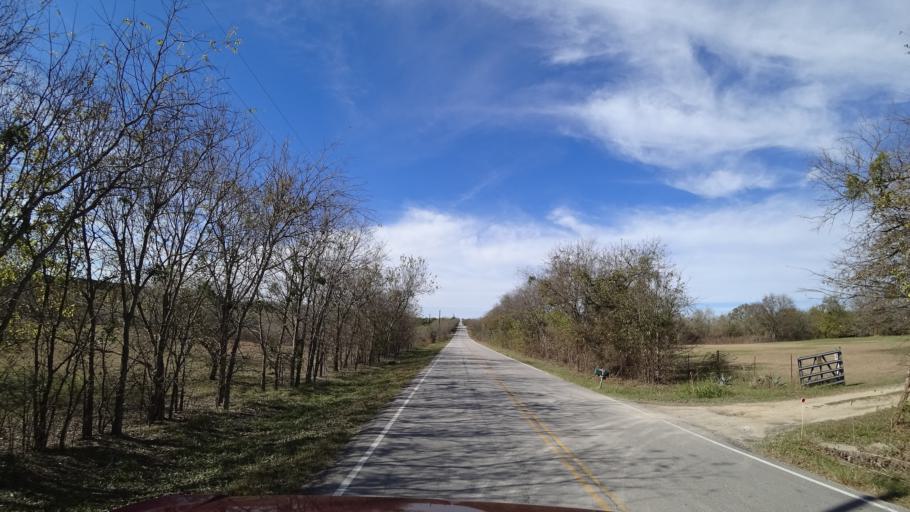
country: US
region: Texas
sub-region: Travis County
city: Onion Creek
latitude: 30.1021
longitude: -97.7295
